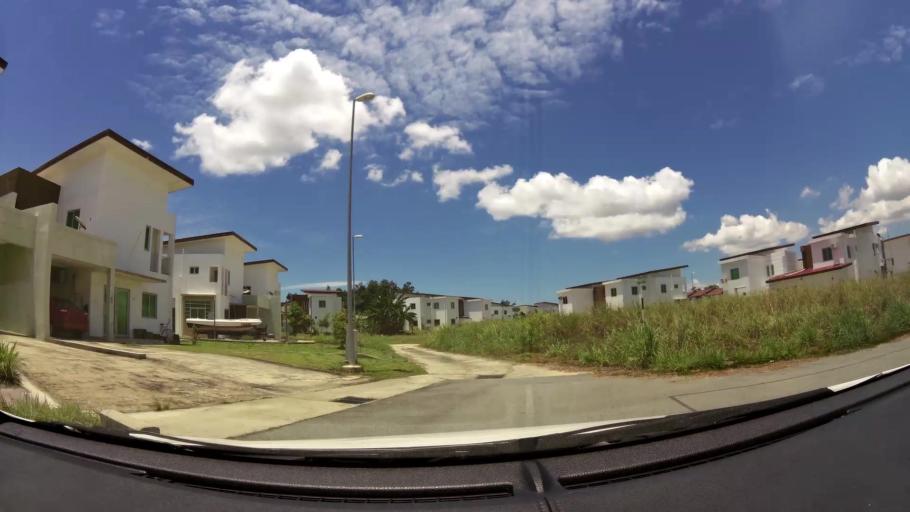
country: BN
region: Brunei and Muara
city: Bandar Seri Begawan
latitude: 5.0058
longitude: 115.0081
